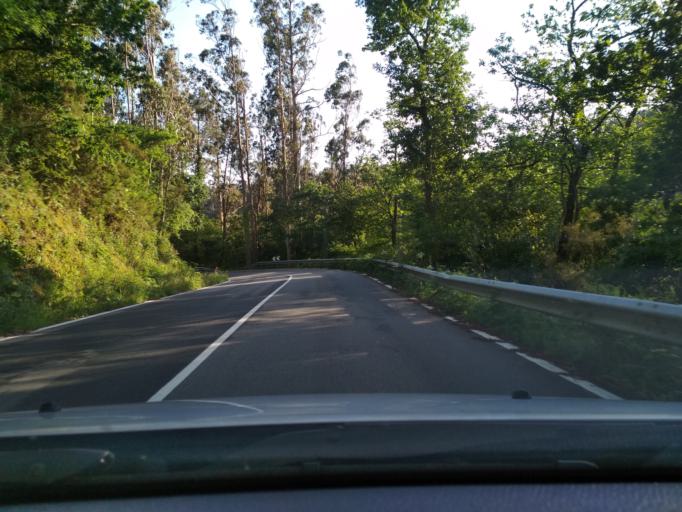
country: ES
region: Galicia
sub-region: Provincia da Coruna
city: Outes
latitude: 42.8990
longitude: -8.9336
